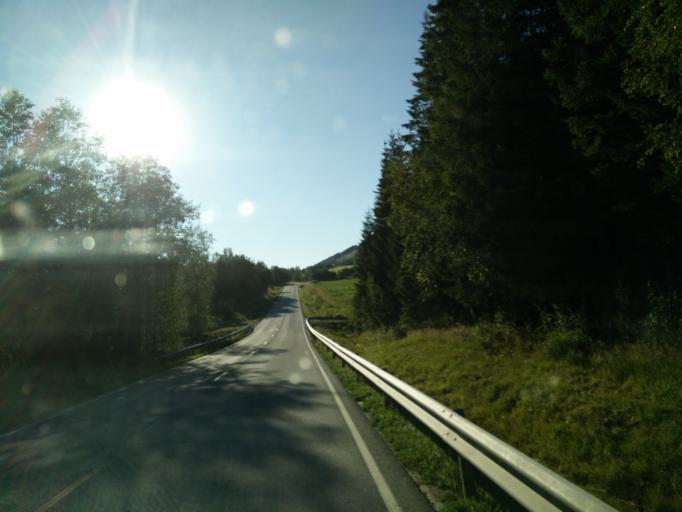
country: NO
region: More og Romsdal
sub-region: Halsa
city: Liaboen
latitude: 63.0720
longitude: 8.2789
